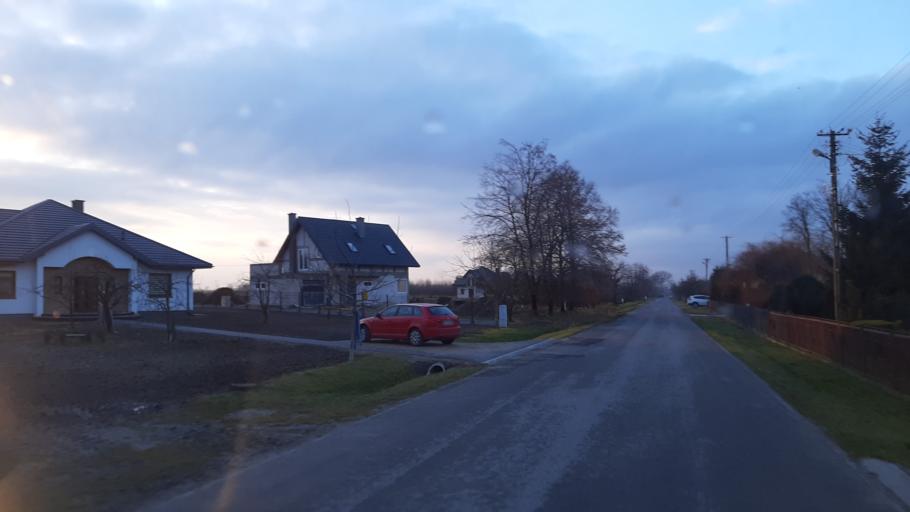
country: PL
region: Lublin Voivodeship
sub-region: Powiat lubelski
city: Garbow
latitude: 51.3801
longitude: 22.4000
